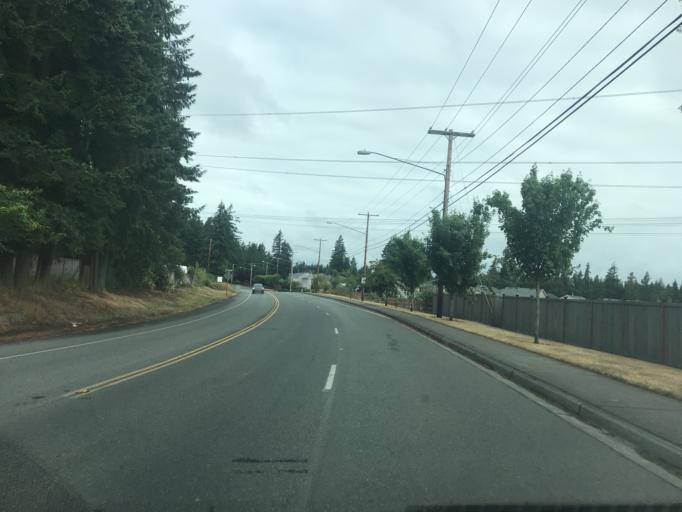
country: US
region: Washington
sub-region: King County
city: Lake Morton-Berrydale
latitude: 47.3414
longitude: -122.0560
